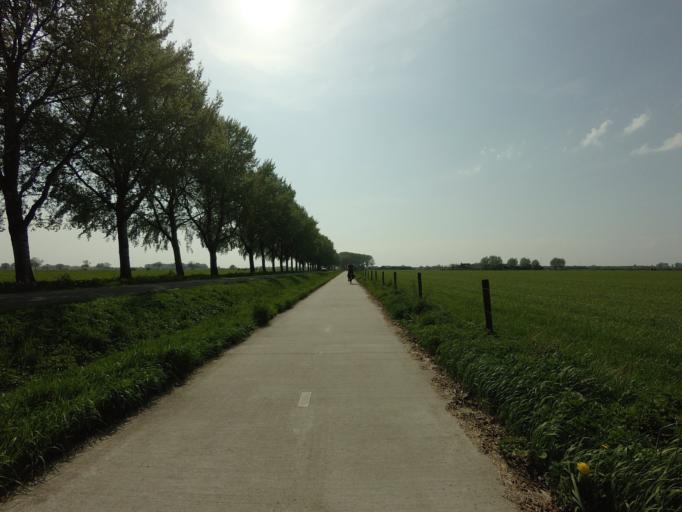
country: NL
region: Utrecht
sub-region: Gemeente Houten
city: Houten
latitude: 52.0200
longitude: 5.2117
